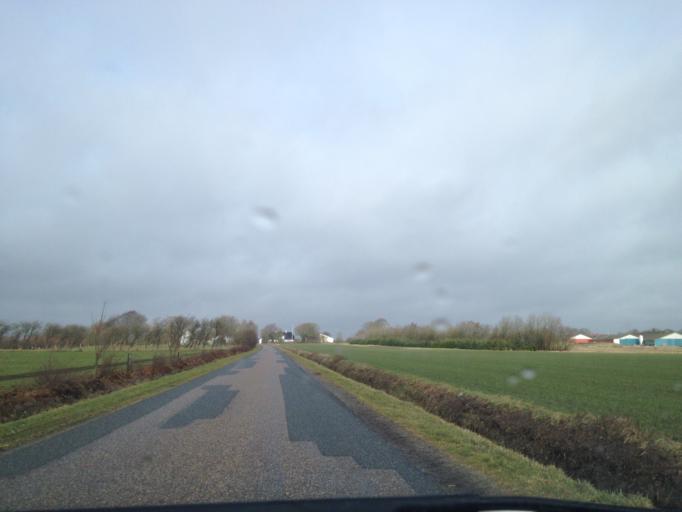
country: DK
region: South Denmark
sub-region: Tonder Kommune
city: Toftlund
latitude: 55.1857
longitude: 9.0089
